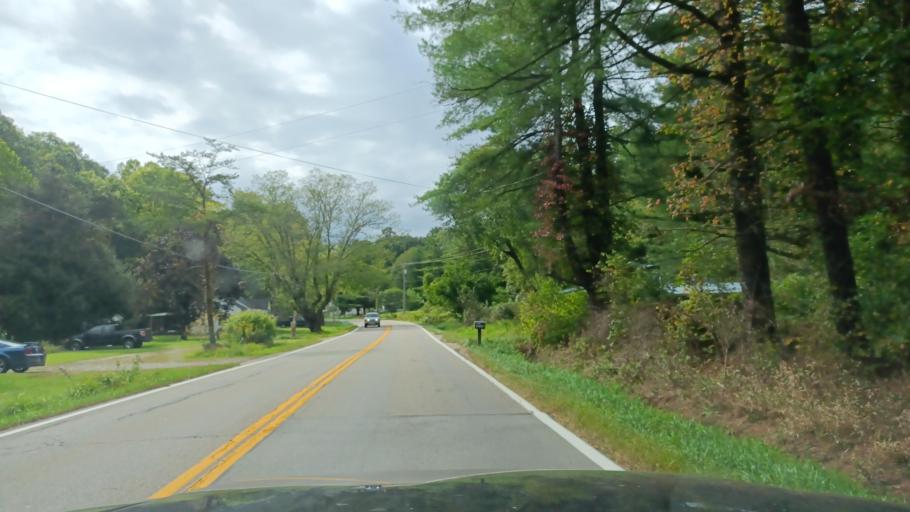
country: US
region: Ohio
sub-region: Vinton County
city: McArthur
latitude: 39.2714
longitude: -82.5690
